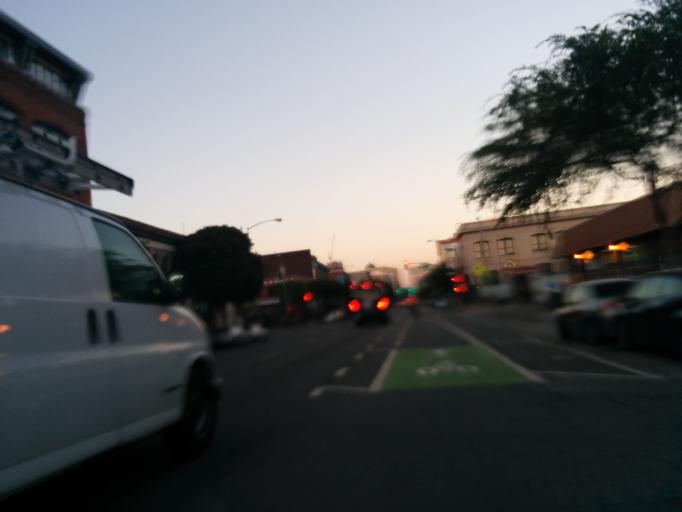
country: US
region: California
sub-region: San Francisco County
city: San Francisco
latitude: 37.7763
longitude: -122.4084
